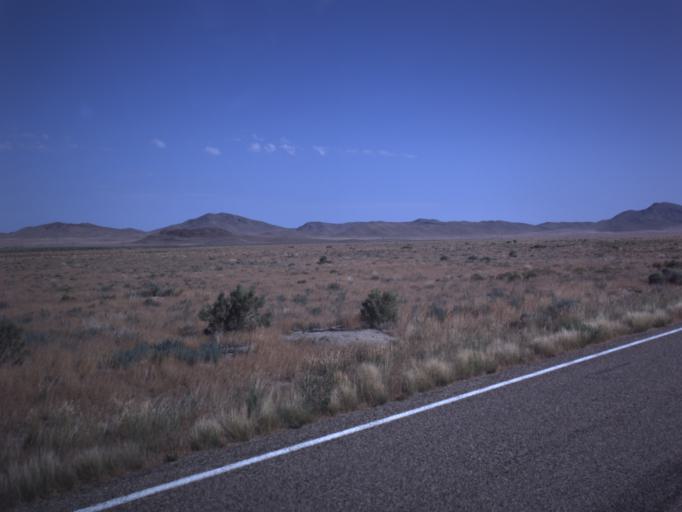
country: US
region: Utah
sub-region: Beaver County
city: Milford
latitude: 38.6561
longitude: -112.9819
